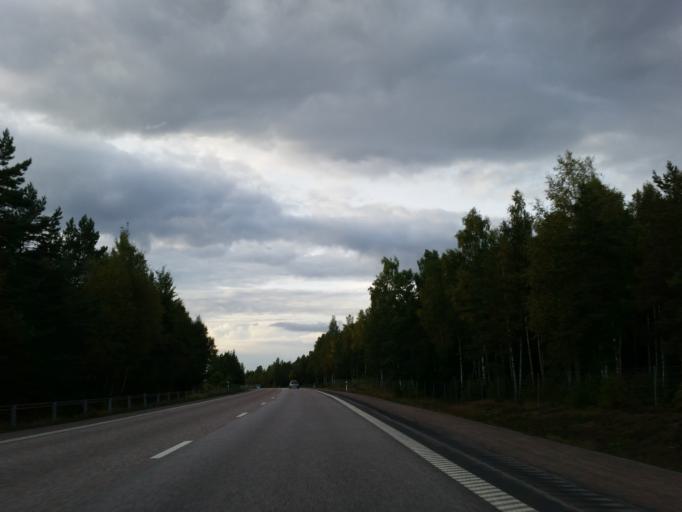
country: SE
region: Stockholm
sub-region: Sigtuna Kommun
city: Marsta
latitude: 59.6945
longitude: 17.8667
